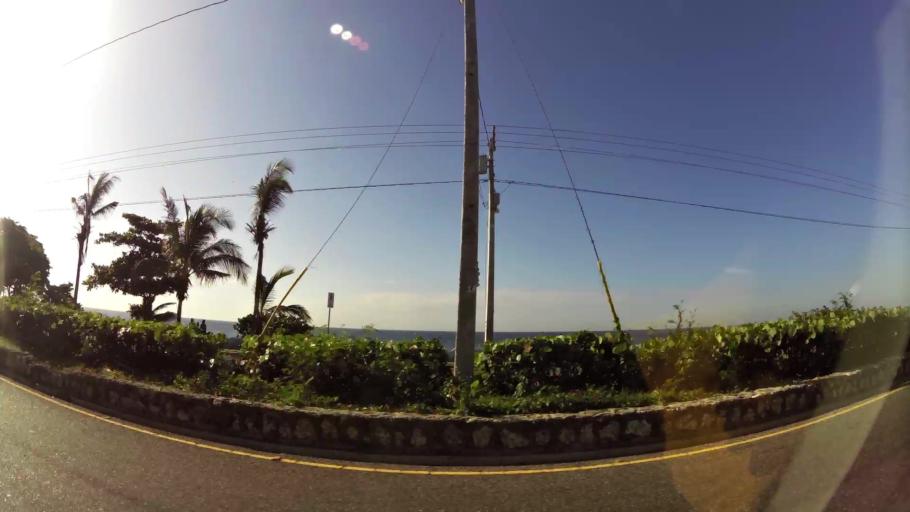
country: DO
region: Santo Domingo
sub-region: Santo Domingo
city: Santo Domingo Este
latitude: 18.4684
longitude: -69.8658
